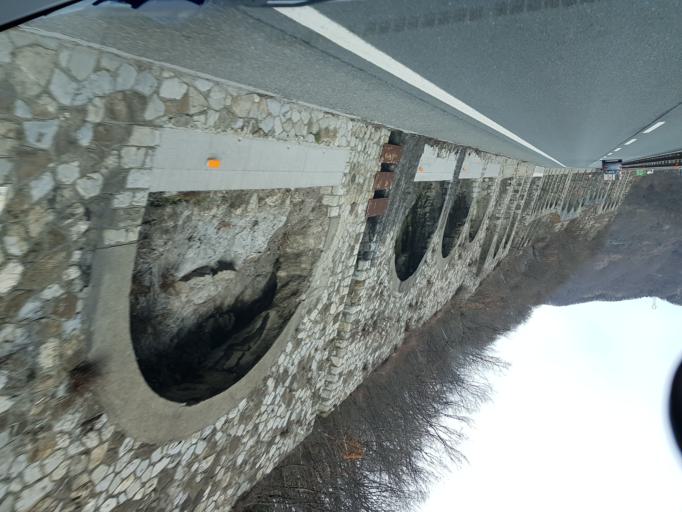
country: IT
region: Liguria
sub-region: Provincia di Genova
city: Ronco Scrivia
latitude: 44.6266
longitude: 8.9475
